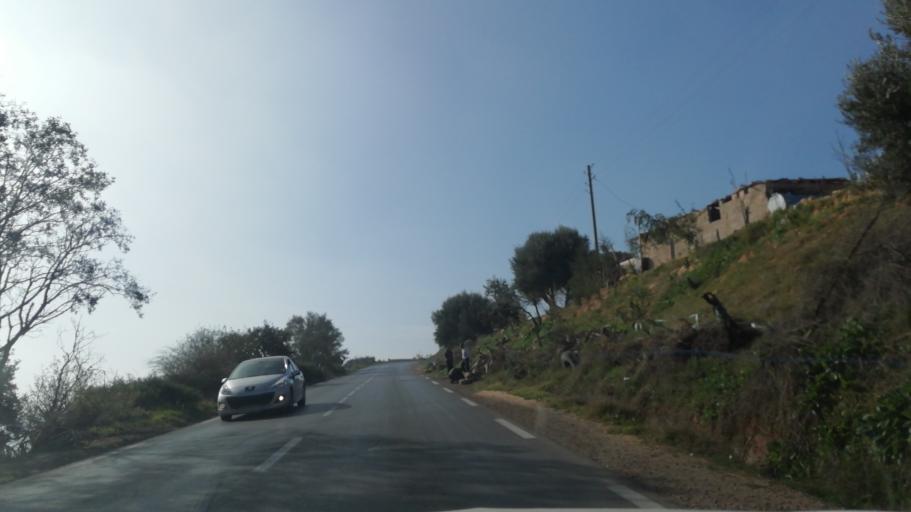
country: DZ
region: Mascara
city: Mascara
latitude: 35.5254
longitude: 0.3519
